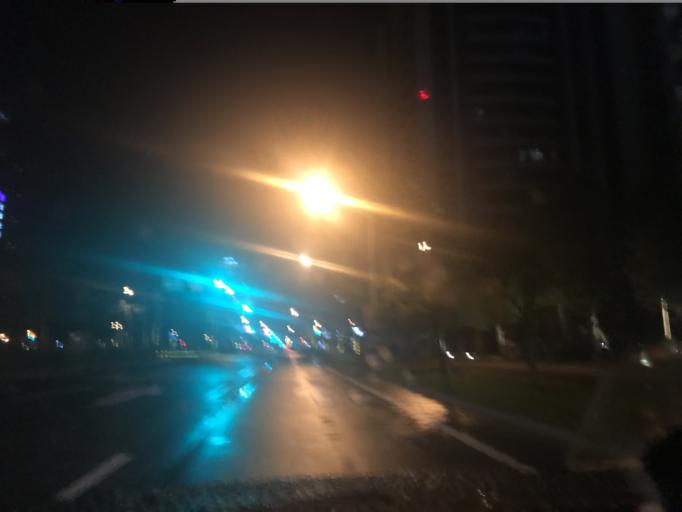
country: TW
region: Taiwan
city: Daxi
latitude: 24.9326
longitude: 121.2809
